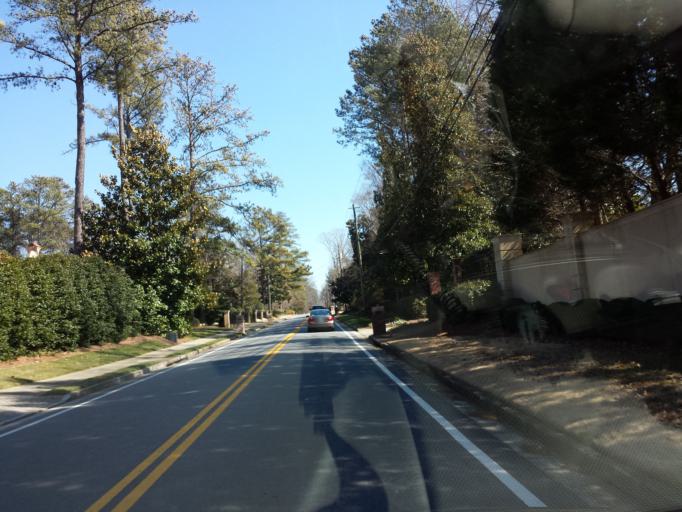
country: US
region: Georgia
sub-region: Fulton County
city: Sandy Springs
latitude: 33.9194
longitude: -84.4118
